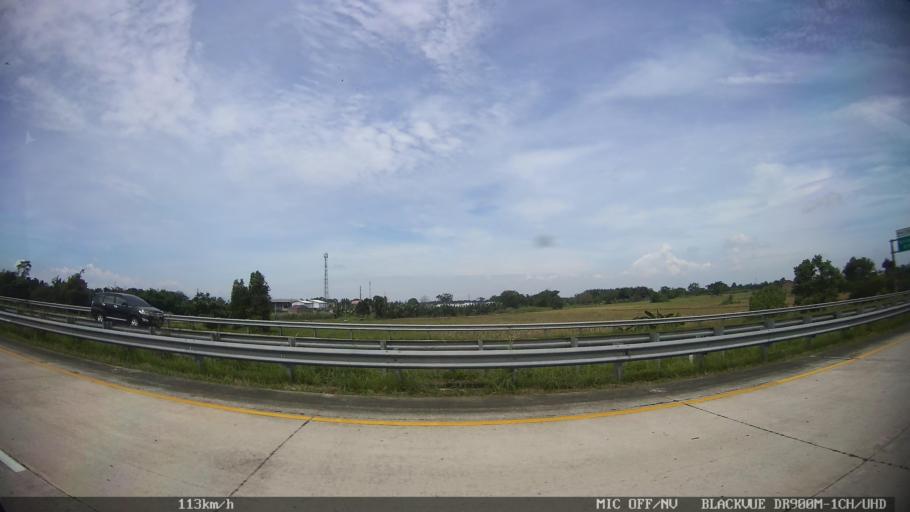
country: ID
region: North Sumatra
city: Percut
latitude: 3.5544
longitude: 98.8523
